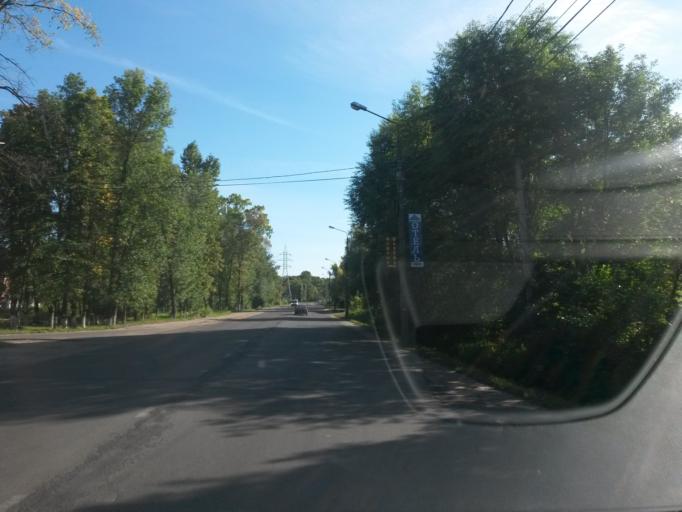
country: RU
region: Jaroslavl
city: Yaroslavl
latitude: 57.5908
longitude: 39.8774
